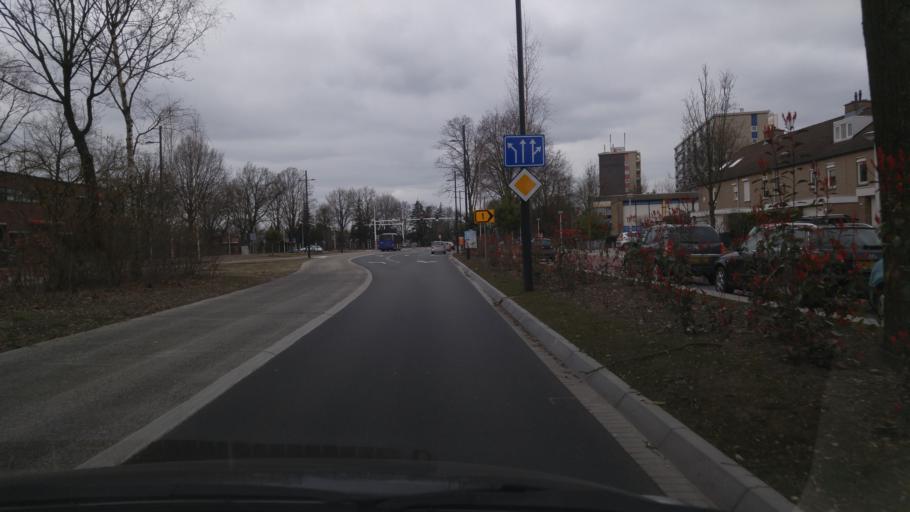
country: NL
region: North Brabant
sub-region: Gemeente Eindhoven
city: Eindhoven
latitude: 51.4779
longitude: 5.4574
